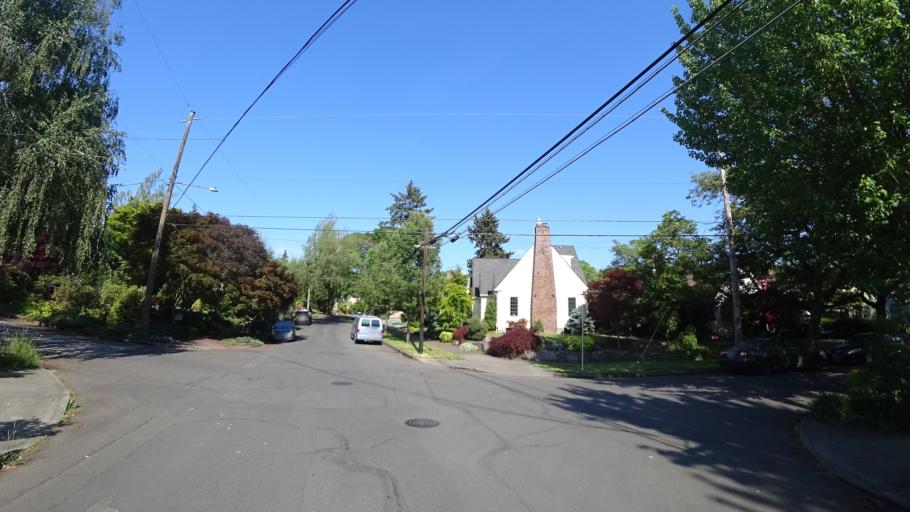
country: US
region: Oregon
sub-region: Multnomah County
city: Portland
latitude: 45.5508
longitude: -122.6454
